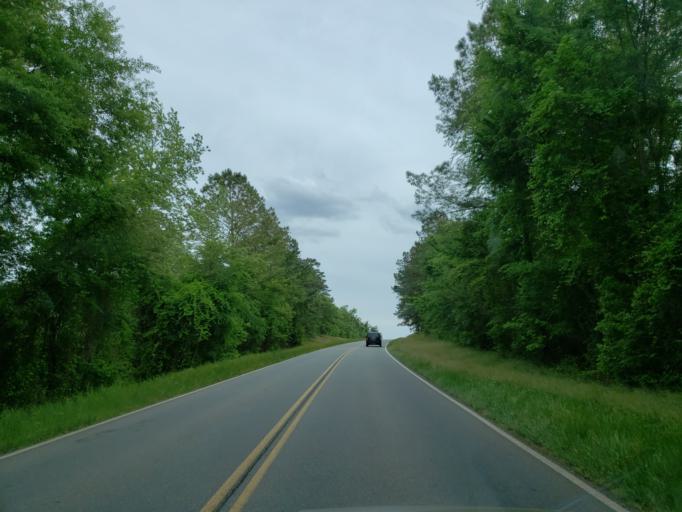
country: US
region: Georgia
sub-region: Macon County
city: Montezuma
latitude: 32.2419
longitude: -83.9614
